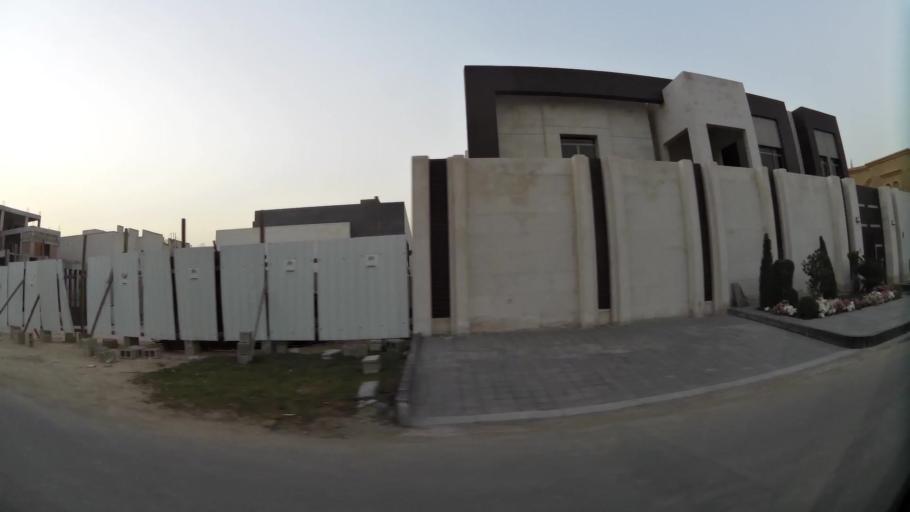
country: QA
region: Baladiyat ar Rayyan
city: Ar Rayyan
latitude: 25.2534
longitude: 51.4646
